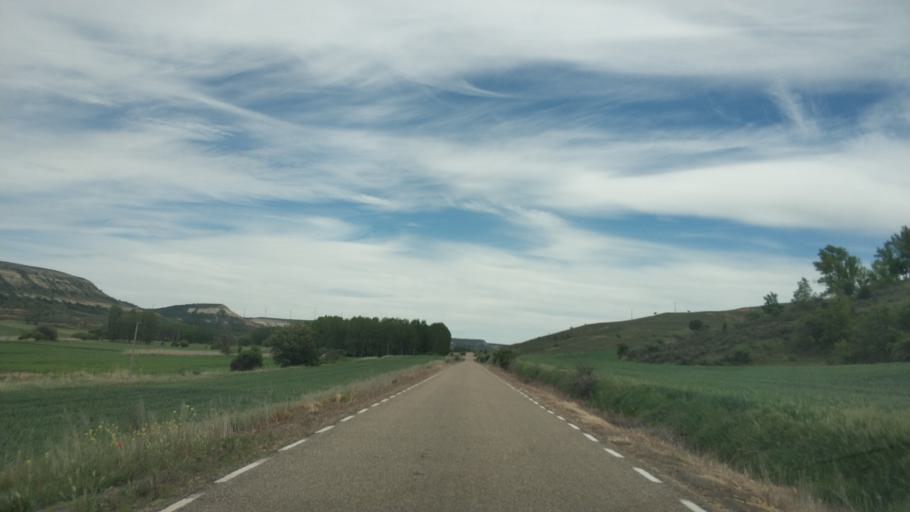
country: ES
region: Castille and Leon
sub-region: Provincia de Soria
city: Caltojar
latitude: 41.4293
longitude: -2.7940
